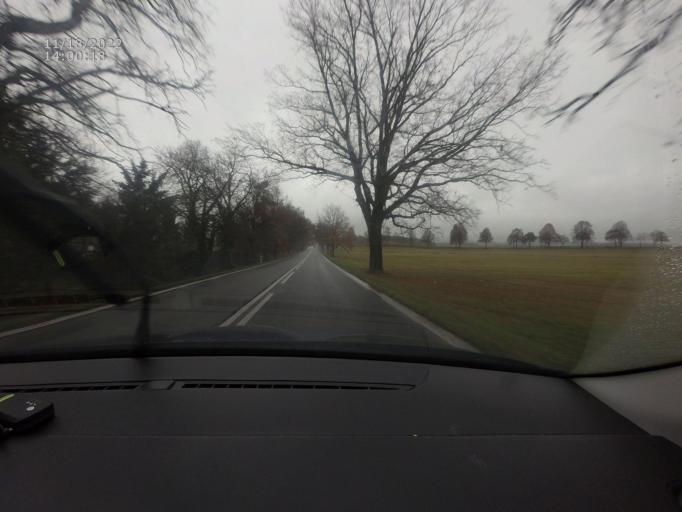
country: CZ
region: Jihocesky
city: Mirotice
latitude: 49.3540
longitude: 14.0171
